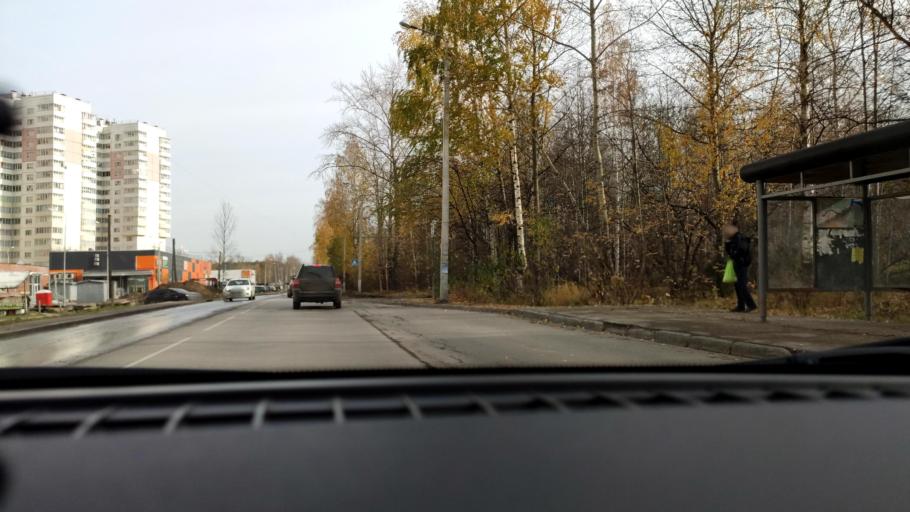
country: RU
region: Perm
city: Polazna
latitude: 58.1321
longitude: 56.3988
